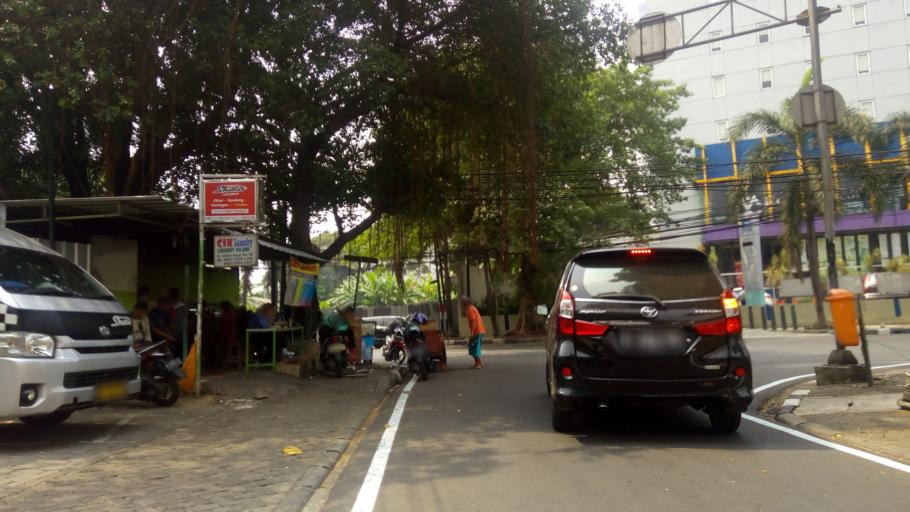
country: ID
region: Jakarta Raya
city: Jakarta
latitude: -6.1917
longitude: 106.8381
